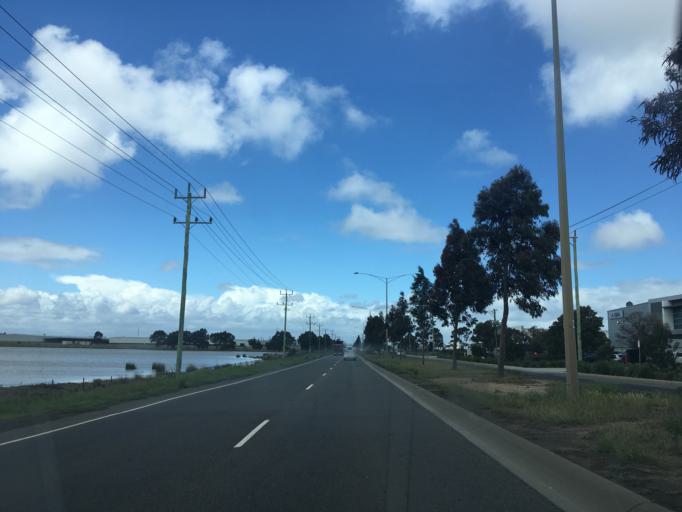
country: AU
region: Victoria
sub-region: Brimbank
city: Derrimut
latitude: -37.8137
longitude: 144.7911
